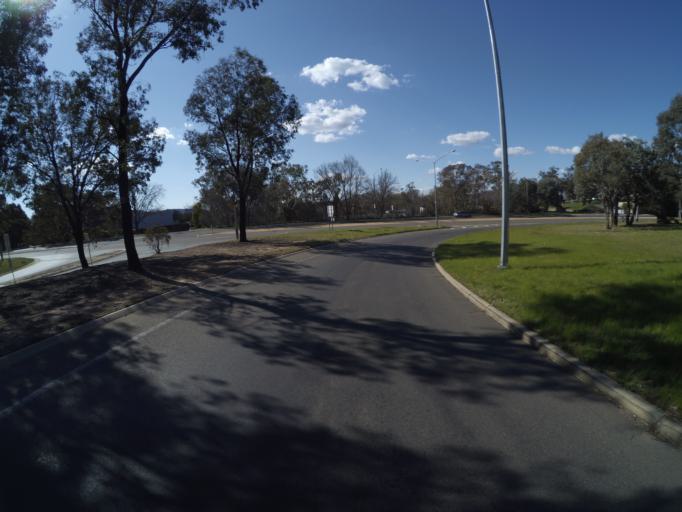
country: AU
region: Australian Capital Territory
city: Forrest
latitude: -35.3045
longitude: 149.1234
